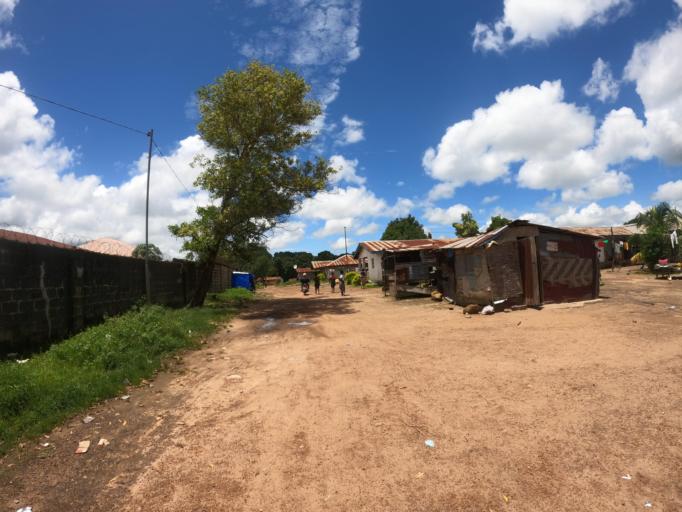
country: SL
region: Northern Province
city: Makeni
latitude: 8.8919
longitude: -12.0689
